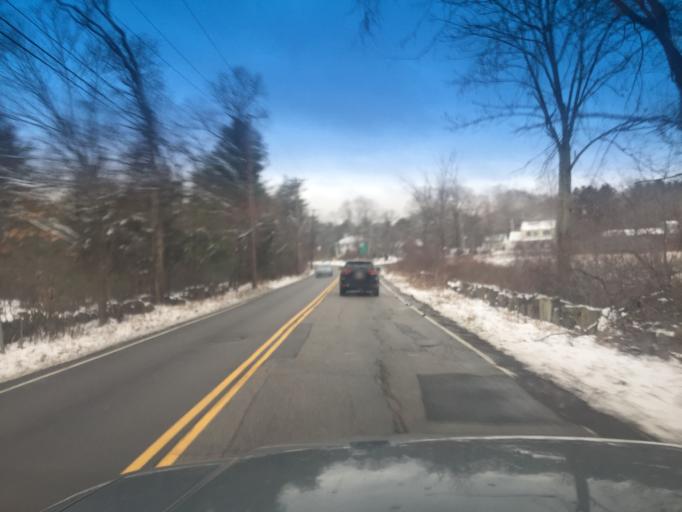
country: US
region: Massachusetts
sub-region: Norfolk County
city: Millis
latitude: 42.1847
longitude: -71.3645
